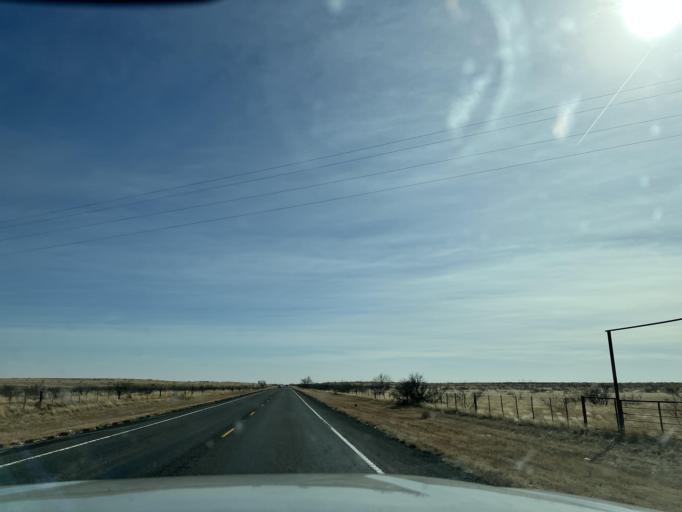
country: US
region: Texas
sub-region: Andrews County
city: Andrews
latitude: 32.4811
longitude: -102.4762
